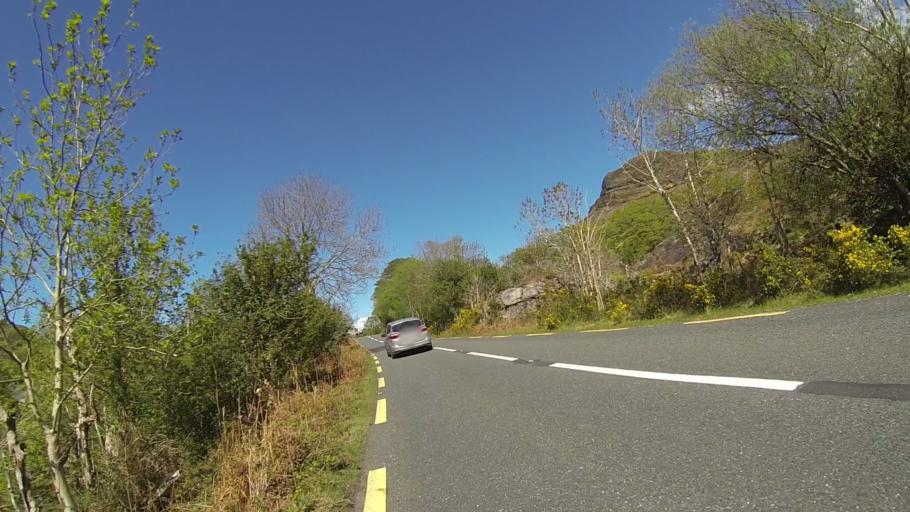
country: IE
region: Munster
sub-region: Ciarrai
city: Cill Airne
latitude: 51.9912
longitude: -9.5536
